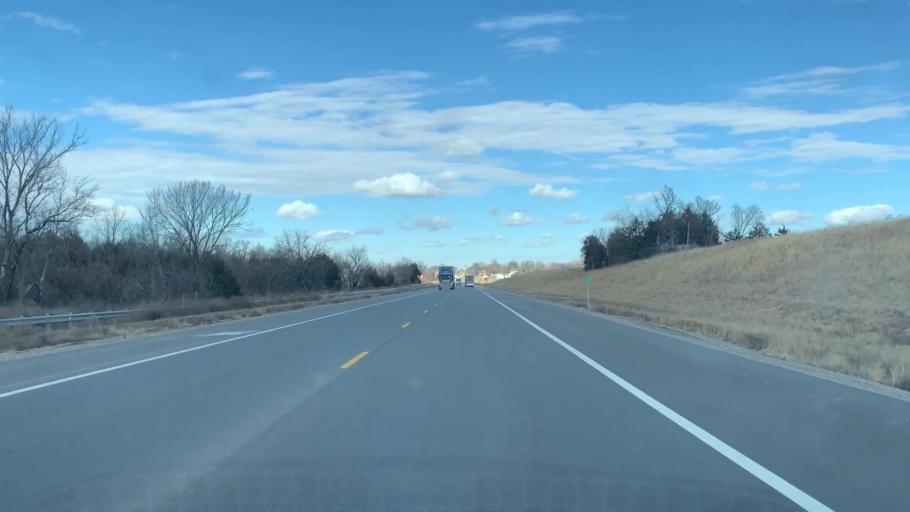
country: US
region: Kansas
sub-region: Crawford County
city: Pittsburg
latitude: 37.3322
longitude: -94.8321
